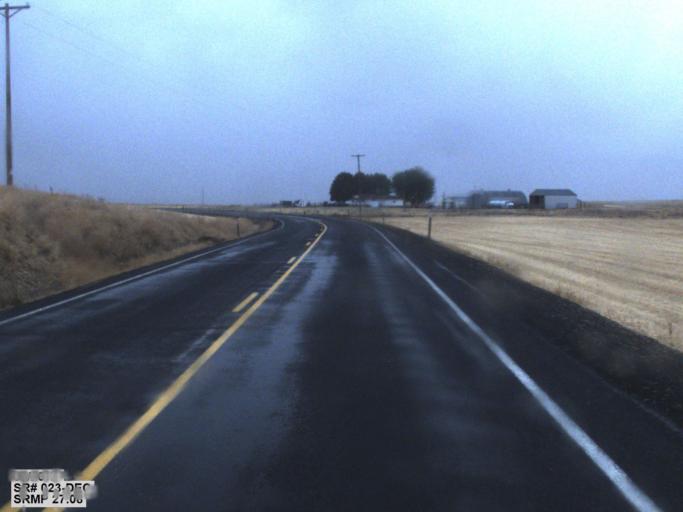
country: US
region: Washington
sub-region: Spokane County
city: Cheney
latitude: 47.1150
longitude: -117.8231
